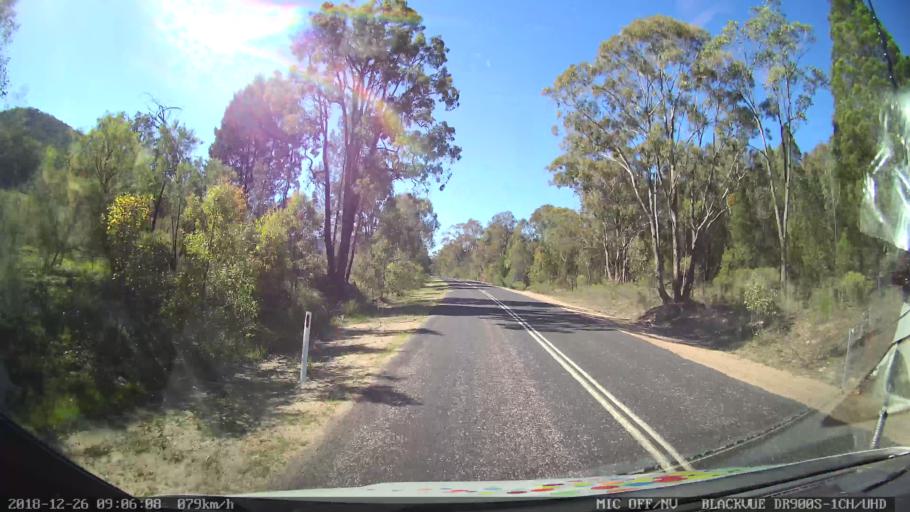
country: AU
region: New South Wales
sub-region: Mid-Western Regional
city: Kandos
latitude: -32.6906
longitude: 150.0045
